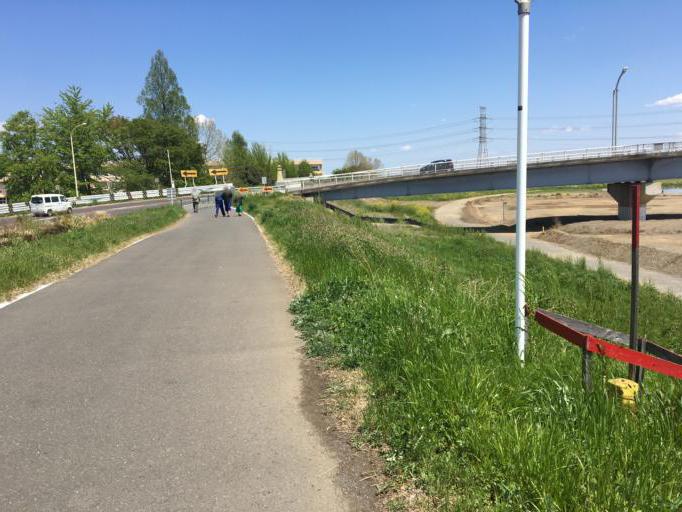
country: JP
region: Saitama
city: Kawagoe
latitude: 35.9293
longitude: 139.4524
